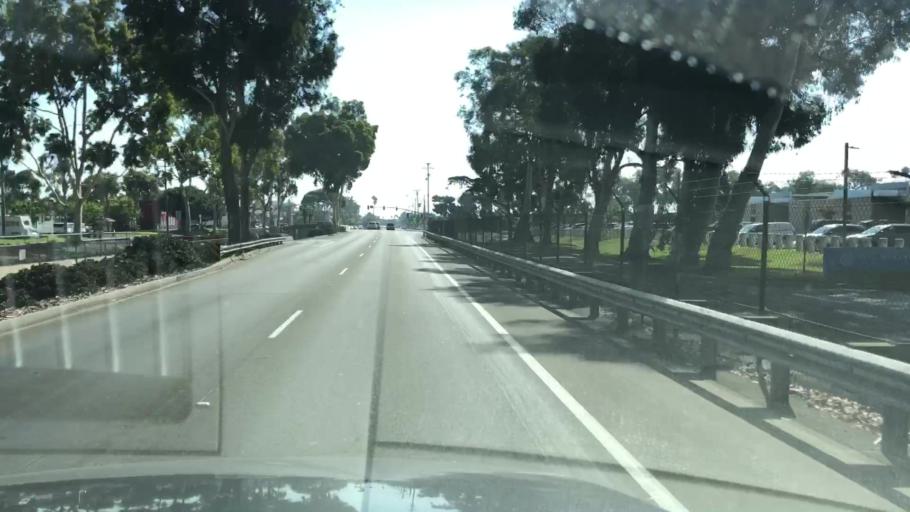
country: US
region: California
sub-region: Ventura County
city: Port Hueneme
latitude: 34.1756
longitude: -119.1975
